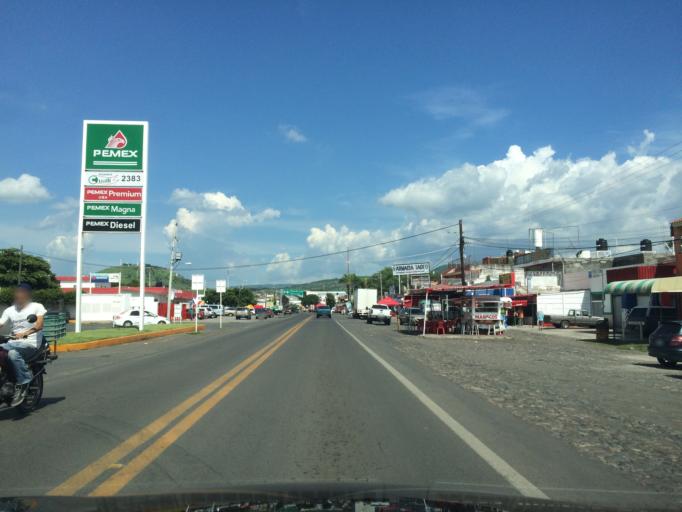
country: MX
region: Nayarit
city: Ixtlan del Rio
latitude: 21.0372
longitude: -104.3791
